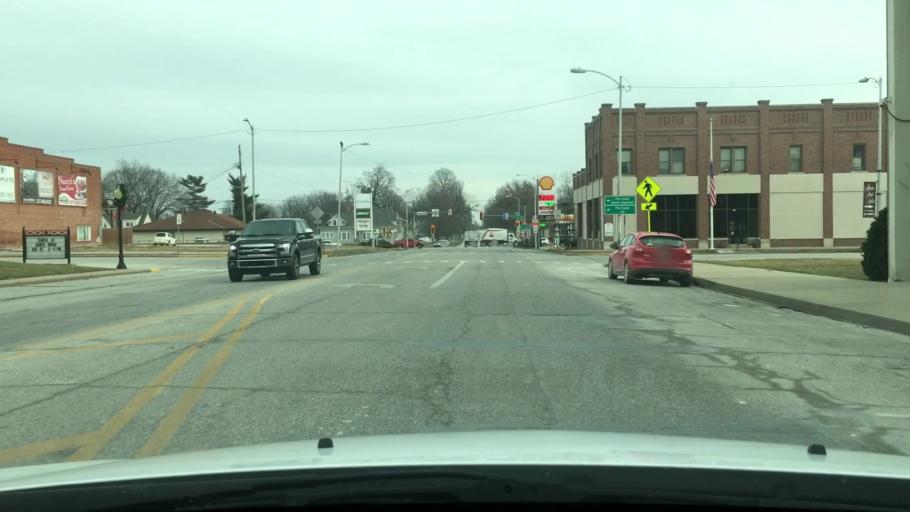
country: US
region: Illinois
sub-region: Pike County
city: Pittsfield
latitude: 39.6068
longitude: -90.8052
